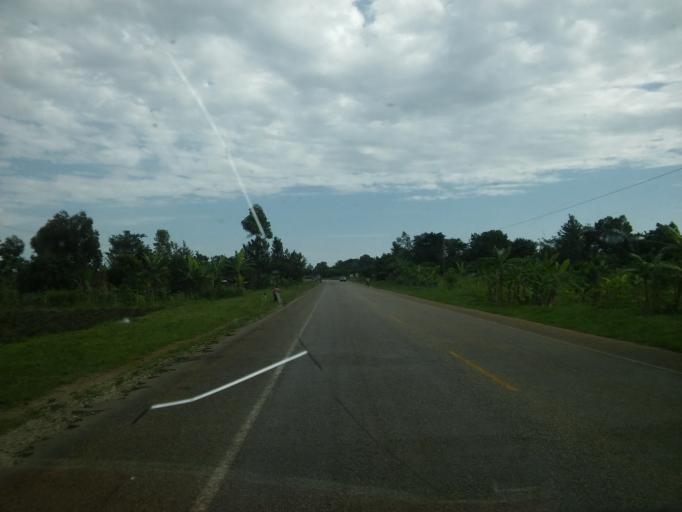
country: UG
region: Eastern Region
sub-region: Mbale District
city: Mbale
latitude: 1.1672
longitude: 34.1566
